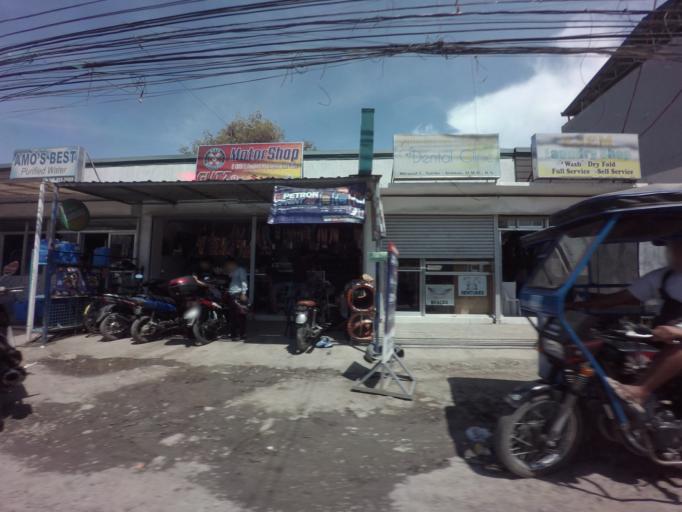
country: PH
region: Calabarzon
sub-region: Province of Rizal
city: Las Pinas
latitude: 14.4655
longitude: 120.9723
